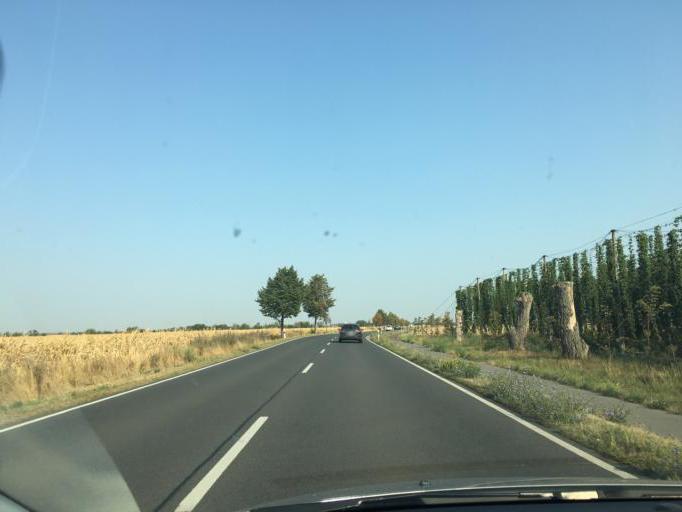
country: DE
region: Saxony-Anhalt
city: Gorzig
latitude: 51.7175
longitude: 12.0284
